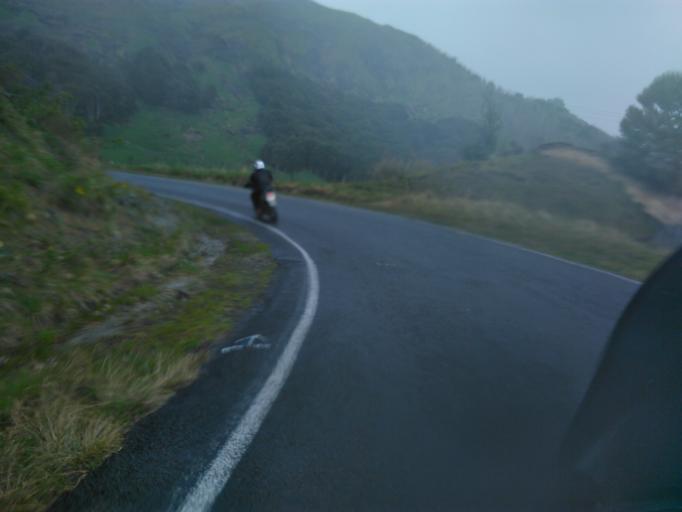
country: NZ
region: Gisborne
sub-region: Gisborne District
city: Gisborne
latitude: -38.6689
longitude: 177.7142
